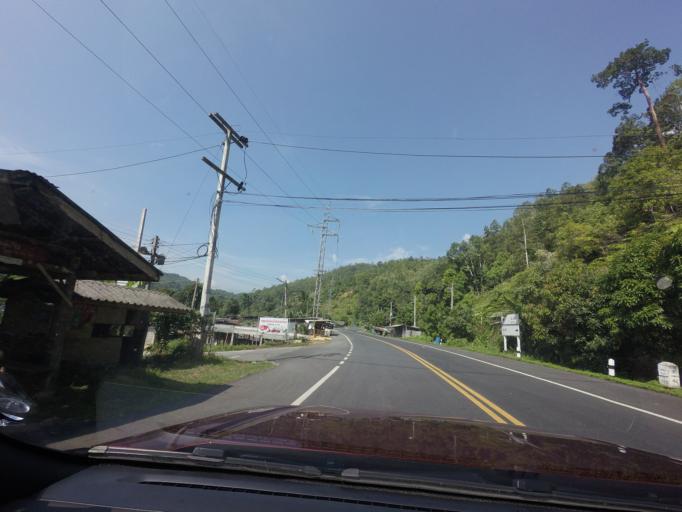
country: TH
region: Yala
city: Than To
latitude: 5.9741
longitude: 101.2008
